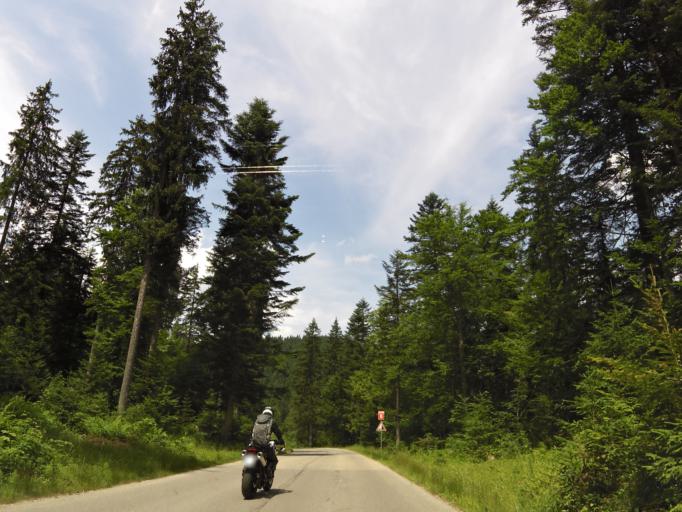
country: AT
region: Tyrol
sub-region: Politischer Bezirk Kitzbuhel
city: Waidring
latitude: 47.6612
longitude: 12.5693
